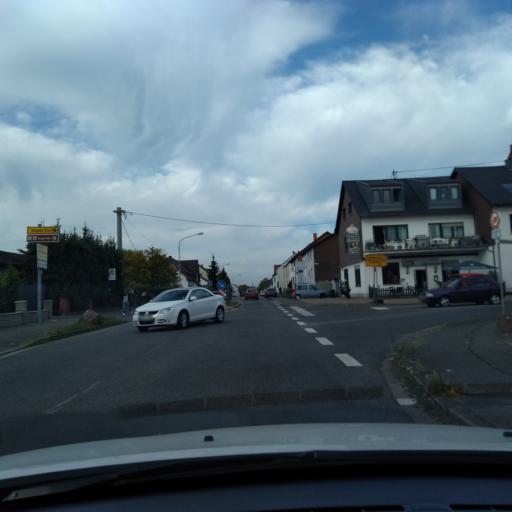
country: DE
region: Saarland
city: Ensdorf
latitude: 49.3110
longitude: 6.7778
